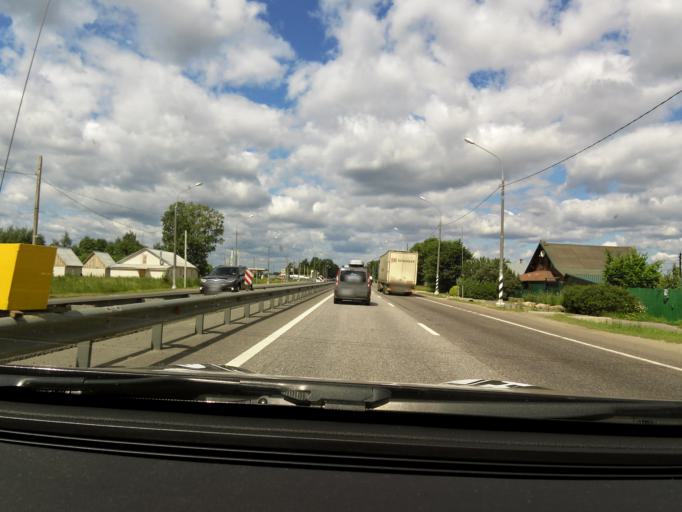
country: RU
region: Tverskaya
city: Torzhok
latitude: 56.9889
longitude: 35.2105
